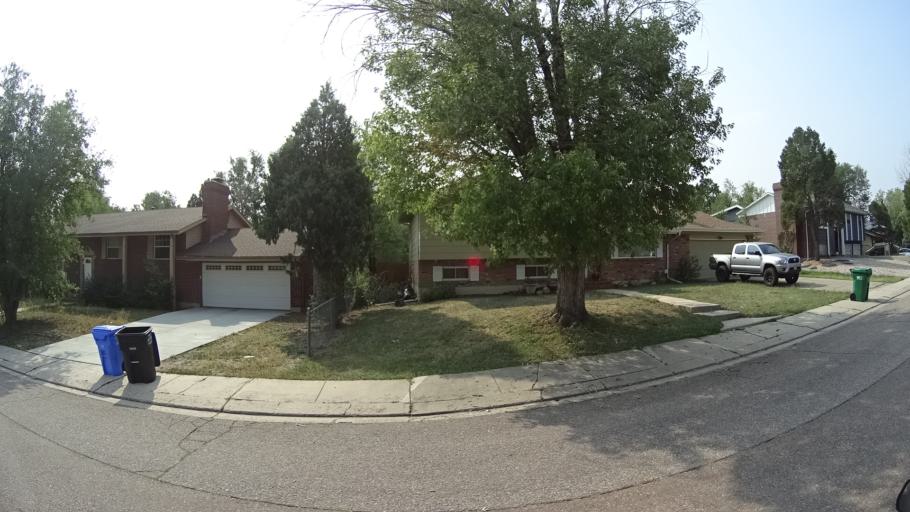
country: US
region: Colorado
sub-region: El Paso County
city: Stratmoor
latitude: 38.8130
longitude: -104.7685
